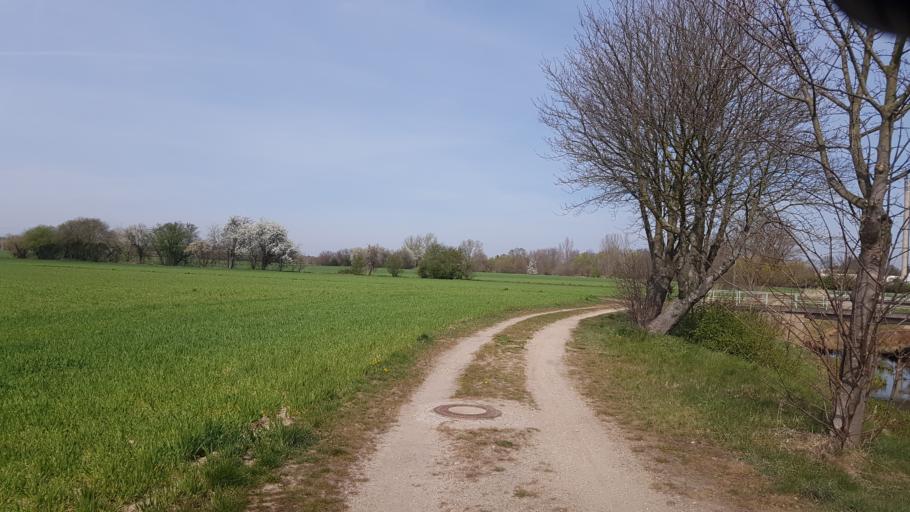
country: DE
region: Brandenburg
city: Doberlug-Kirchhain
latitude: 51.6300
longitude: 13.5554
